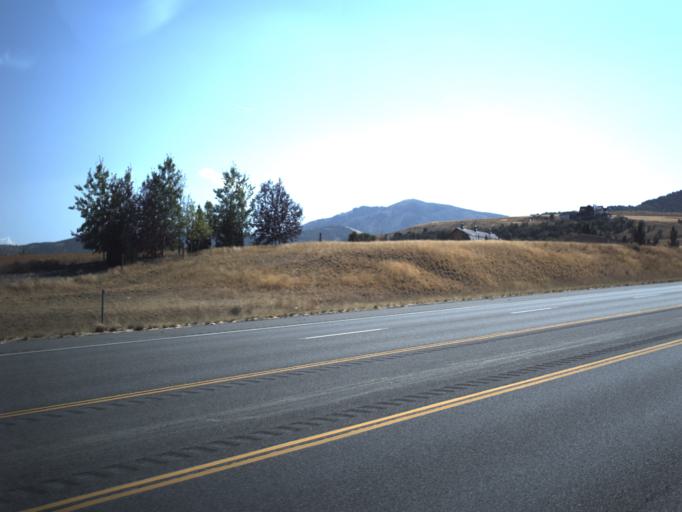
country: US
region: Utah
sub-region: Cache County
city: Wellsville
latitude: 41.6113
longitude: -111.9376
